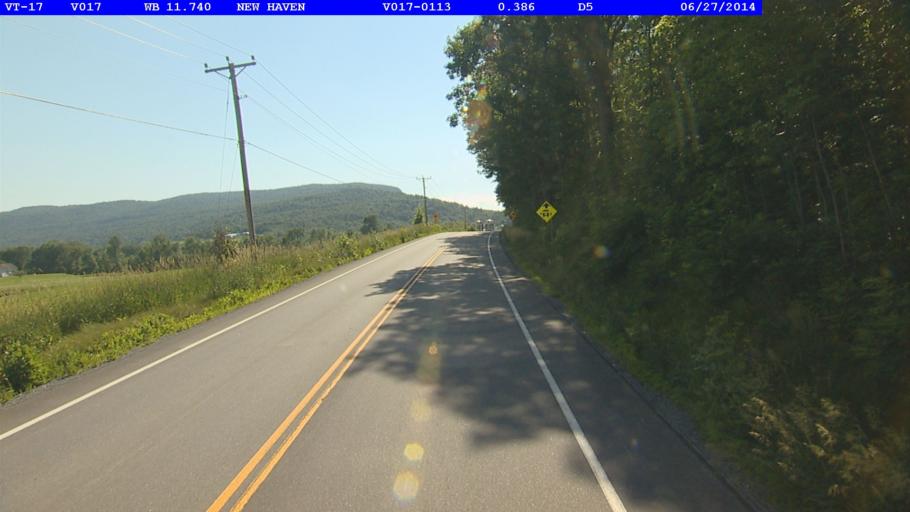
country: US
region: Vermont
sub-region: Addison County
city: Vergennes
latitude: 44.0871
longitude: -73.2390
